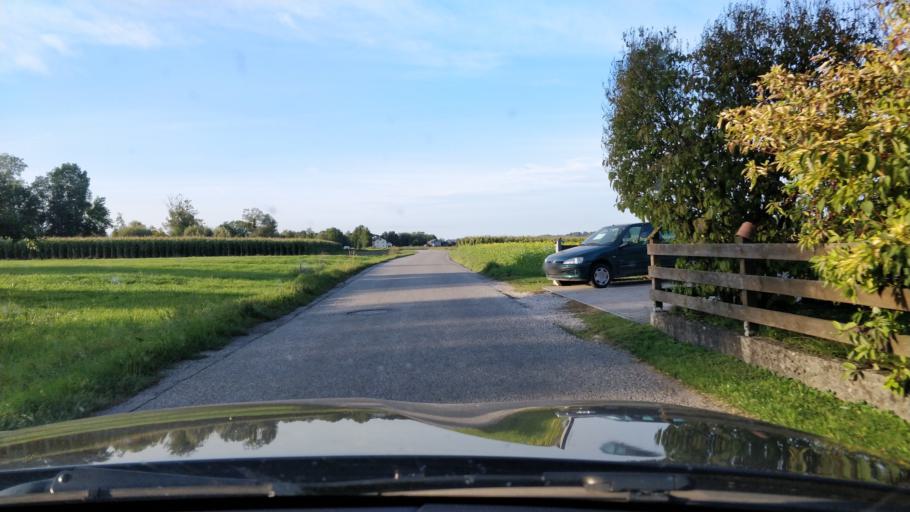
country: AT
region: Upper Austria
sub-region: Politischer Bezirk Braunau am Inn
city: Braunau am Inn
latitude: 48.1655
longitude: 13.1280
